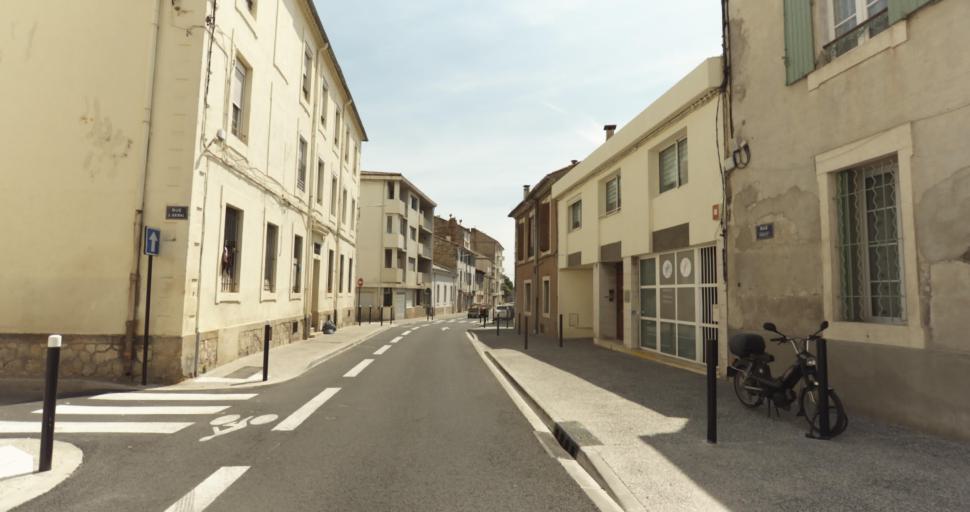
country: FR
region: Languedoc-Roussillon
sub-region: Departement du Gard
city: Nimes
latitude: 43.8443
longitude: 4.3684
